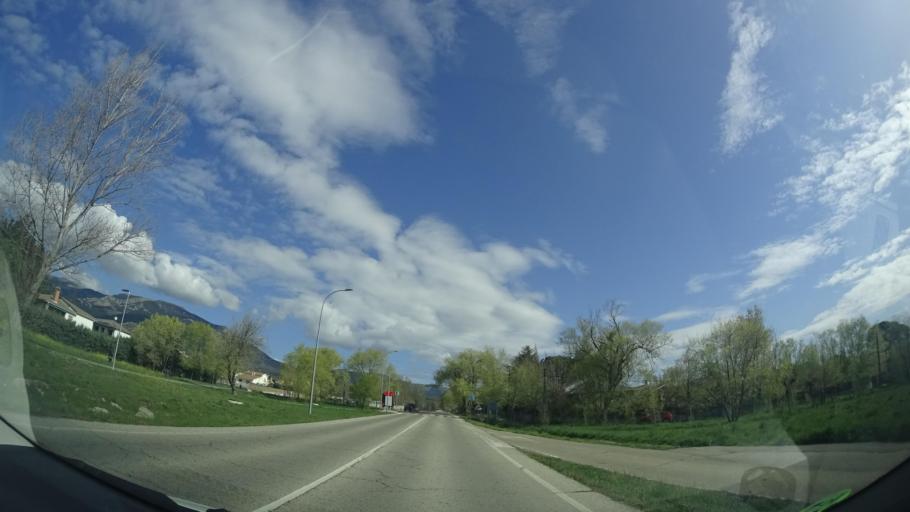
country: ES
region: Madrid
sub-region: Provincia de Madrid
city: Miraflores de la Sierra
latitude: 40.7587
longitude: -3.7827
